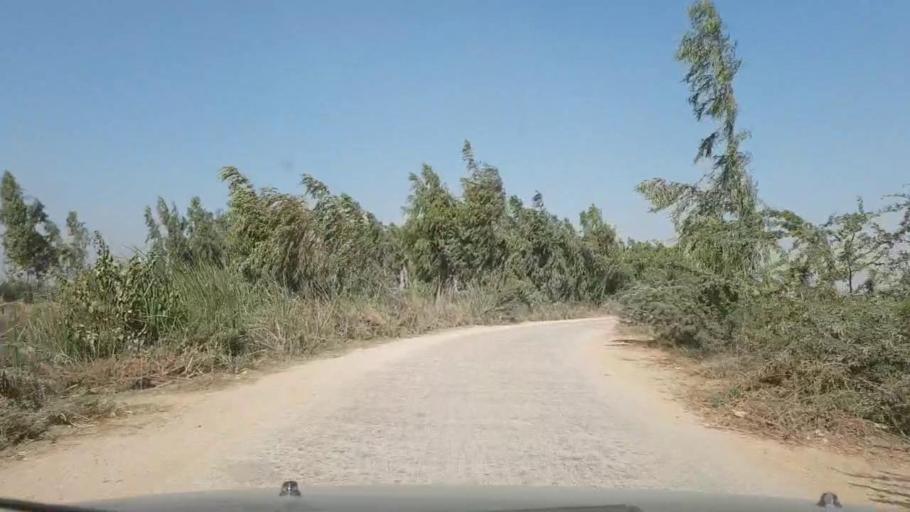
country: PK
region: Sindh
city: Thatta
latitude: 24.7933
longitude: 67.9019
